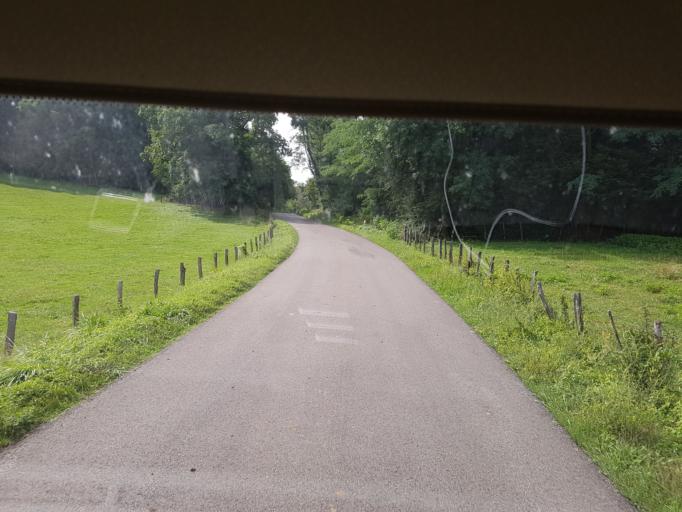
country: FR
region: Rhone-Alpes
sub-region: Departement de l'Ain
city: Poncin
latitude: 46.1211
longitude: 5.3984
